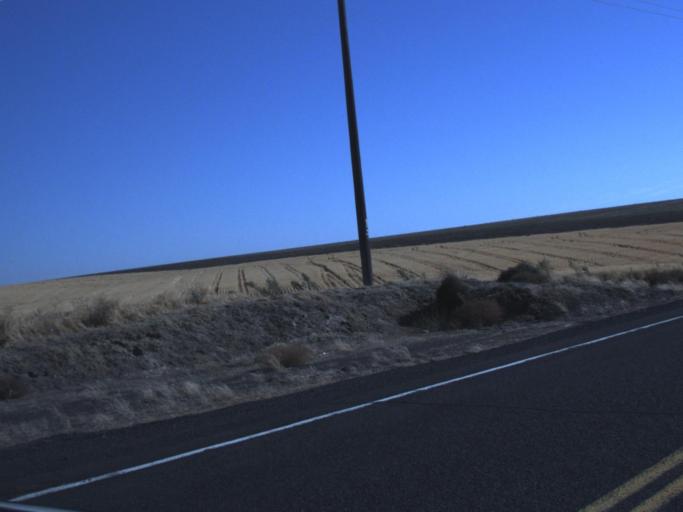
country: US
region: Washington
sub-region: Adams County
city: Ritzville
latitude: 46.8694
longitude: -118.5469
